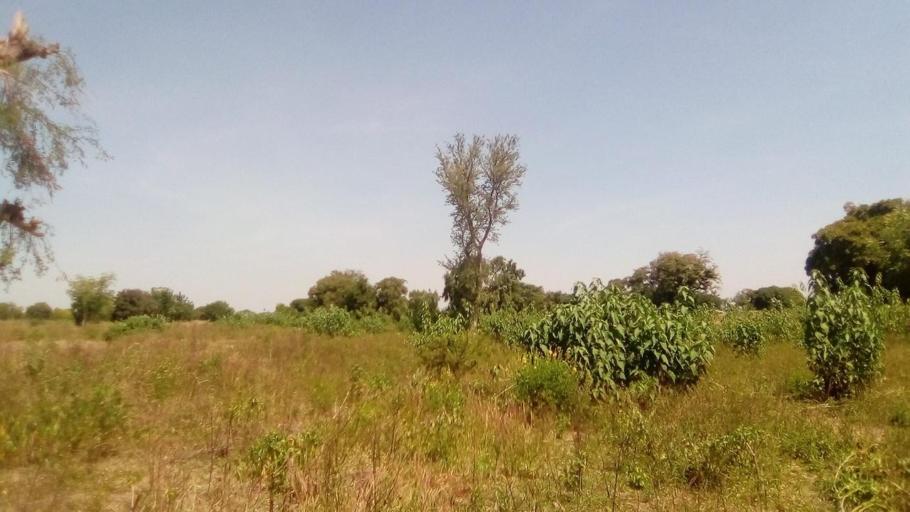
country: GH
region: Upper East
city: Bawku
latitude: 11.0933
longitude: -0.0718
